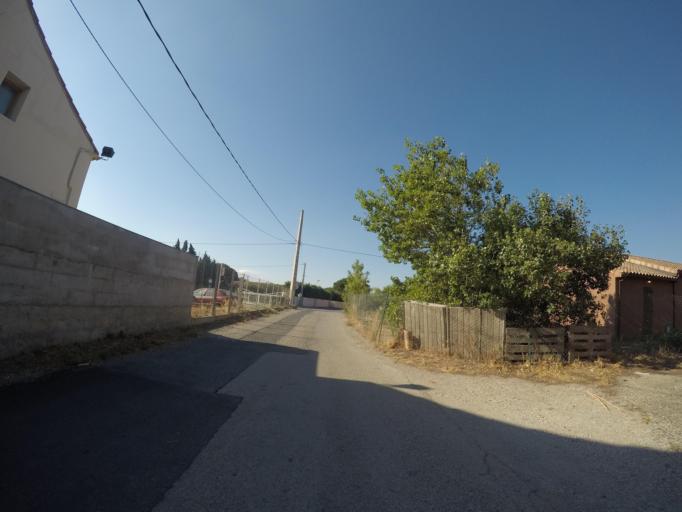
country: FR
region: Languedoc-Roussillon
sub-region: Departement des Pyrenees-Orientales
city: Pezilla-la-Riviere
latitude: 42.6800
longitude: 2.7642
